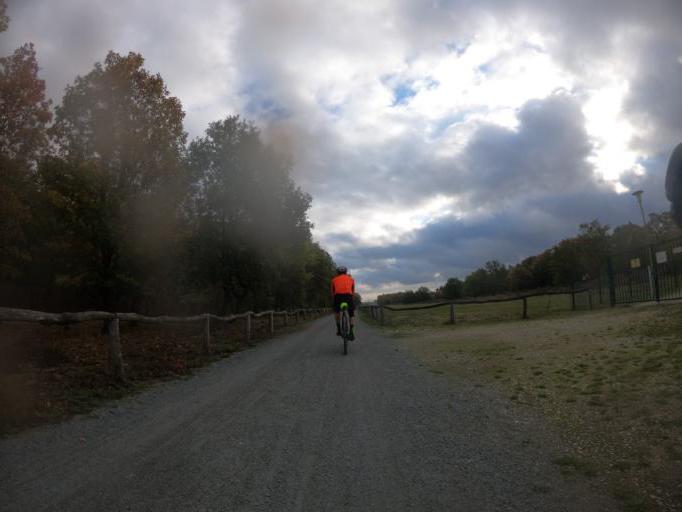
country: DE
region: Hesse
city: Kelsterbach
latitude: 50.0497
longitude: 8.5204
